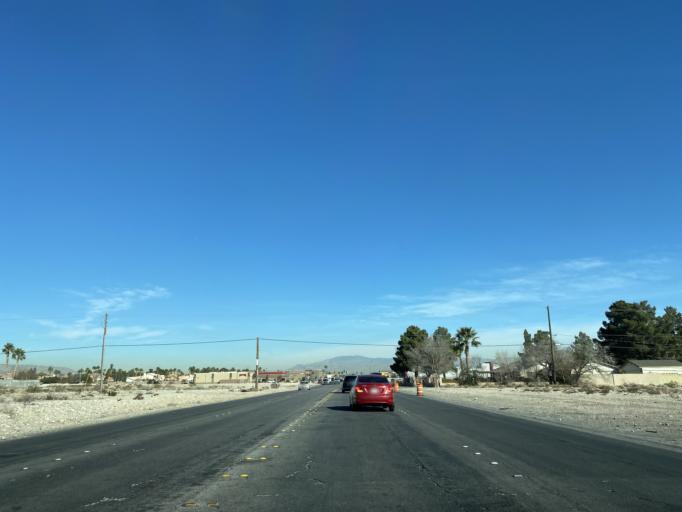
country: US
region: Nevada
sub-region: Clark County
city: Spring Valley
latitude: 36.0820
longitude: -115.2250
